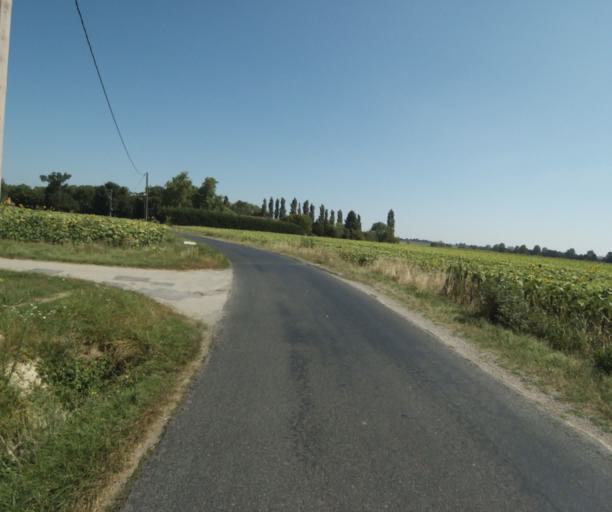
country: FR
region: Midi-Pyrenees
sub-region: Departement de la Haute-Garonne
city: Revel
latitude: 43.5156
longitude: 1.9588
